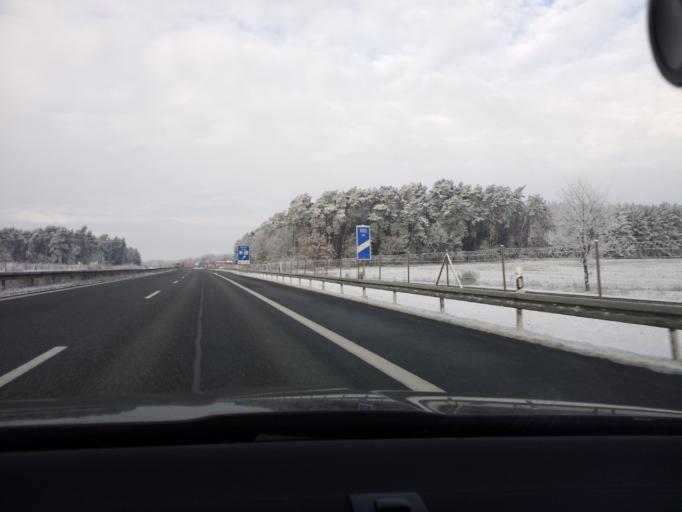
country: DE
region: Mecklenburg-Vorpommern
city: Spornitz
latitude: 53.3655
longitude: 11.7404
